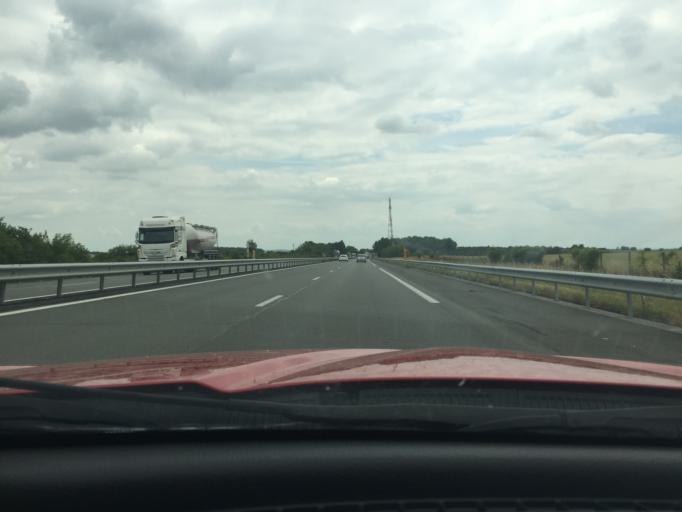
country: FR
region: Picardie
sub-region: Departement de l'Aisne
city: Saint-Erme-Outre-et-Ramecourt
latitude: 49.5290
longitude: 3.8658
